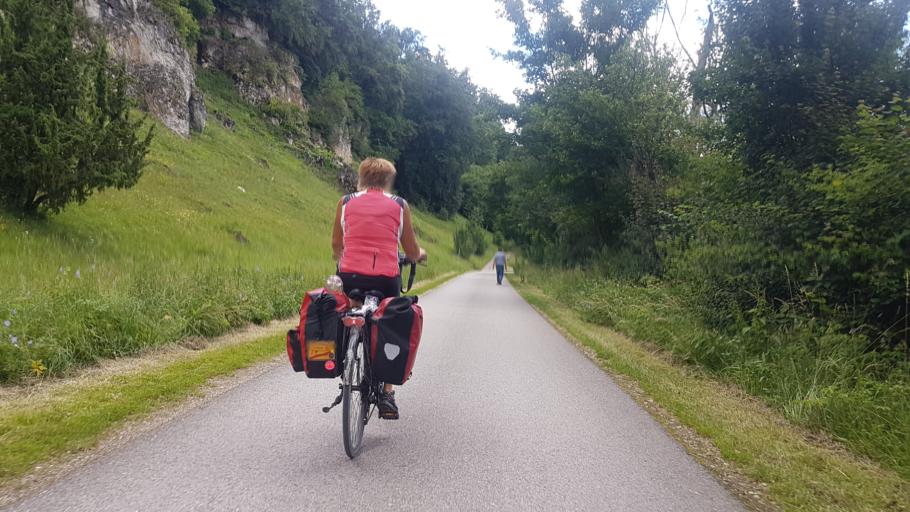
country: DE
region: Bavaria
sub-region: Regierungsbezirk Mittelfranken
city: Solnhofen
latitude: 48.8751
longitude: 11.0225
